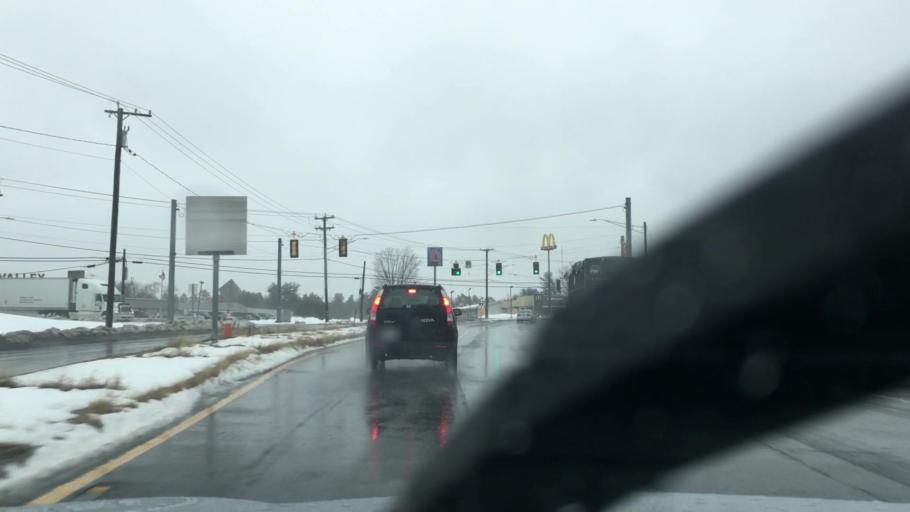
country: US
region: Massachusetts
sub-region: Hampden County
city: North Chicopee
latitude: 42.1649
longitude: -72.5466
